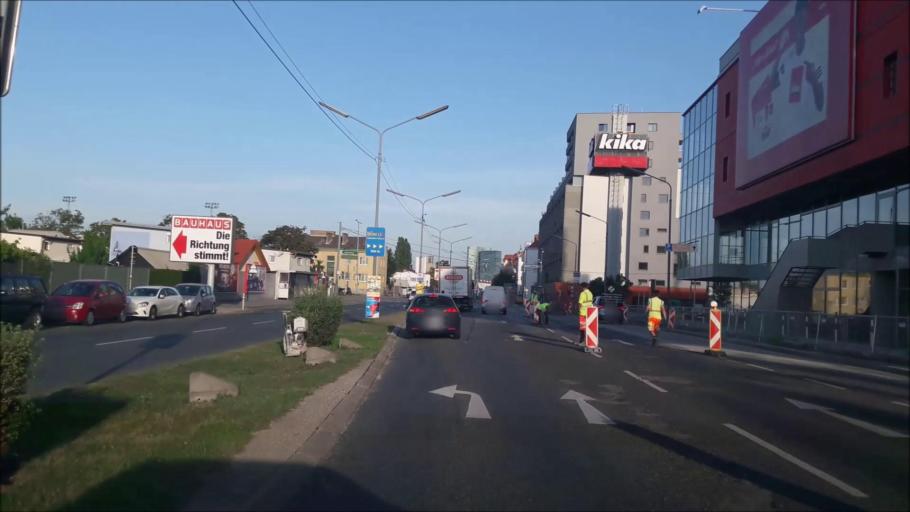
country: AT
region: Vienna
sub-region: Wien Stadt
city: Vienna
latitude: 48.1649
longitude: 16.3699
